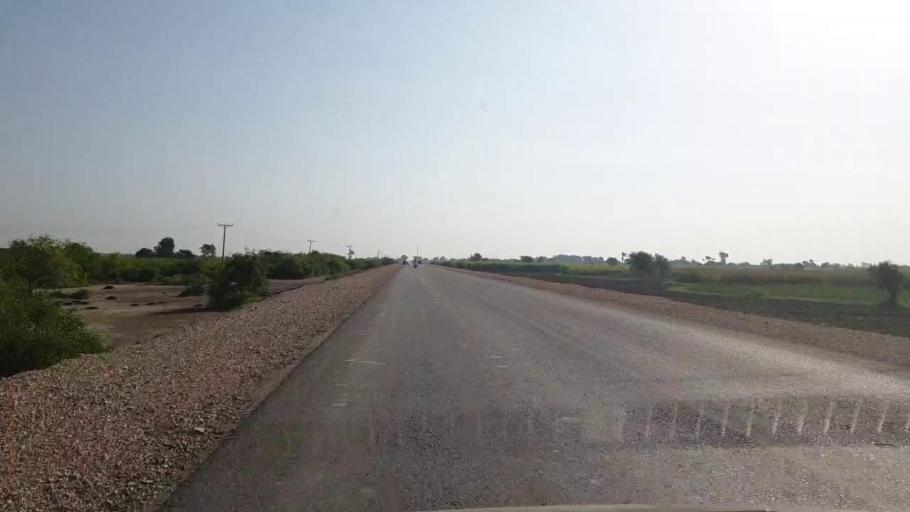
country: PK
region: Sindh
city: Badin
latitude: 24.6589
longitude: 68.9324
